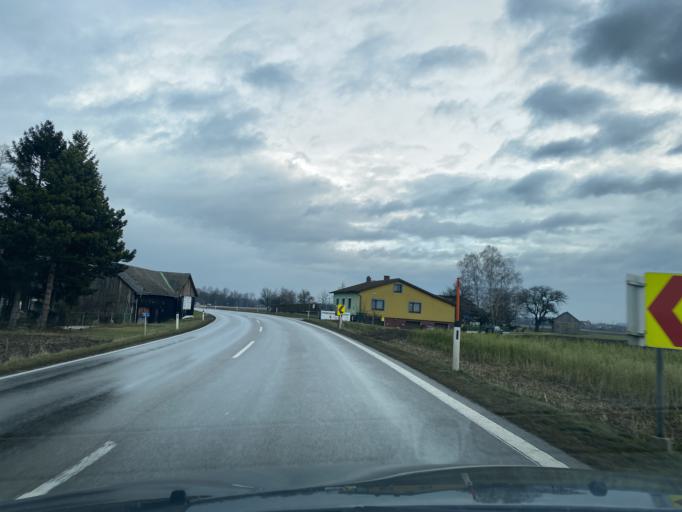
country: AT
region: Lower Austria
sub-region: Politischer Bezirk Sankt Polten
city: Hafnerbach
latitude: 48.1975
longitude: 15.4870
